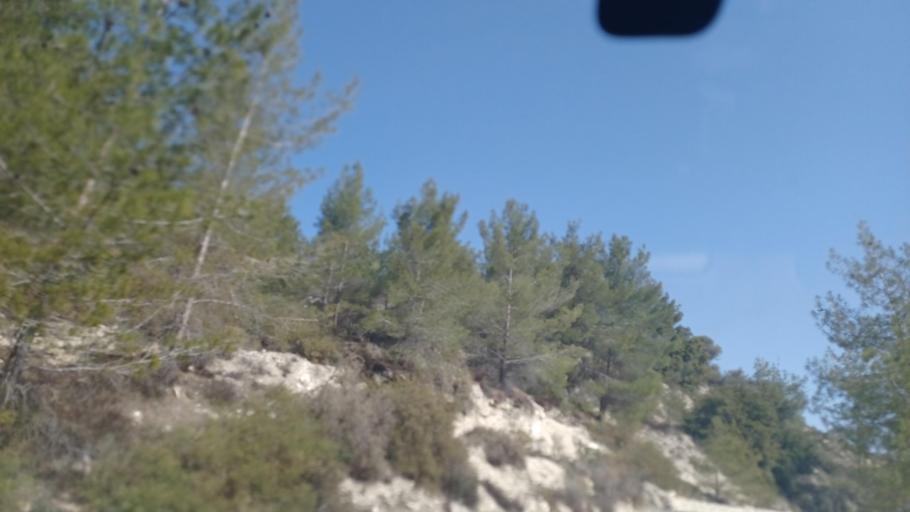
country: CY
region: Limassol
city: Pachna
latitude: 34.8867
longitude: 32.7295
